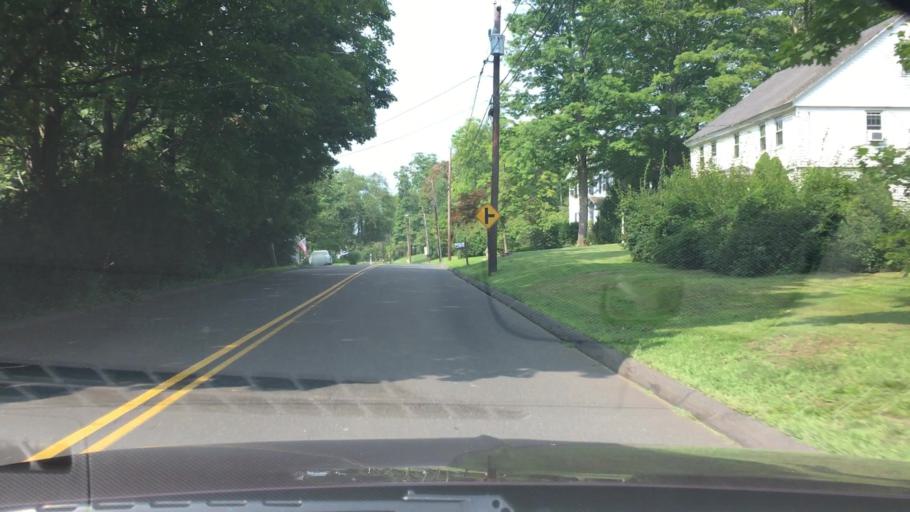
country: US
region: Connecticut
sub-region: Hartford County
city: Kensington
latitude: 41.6110
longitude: -72.7180
